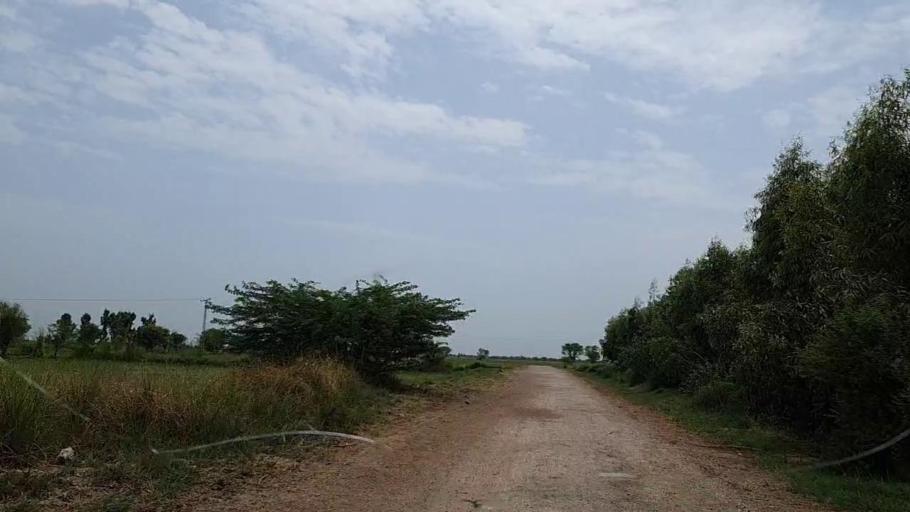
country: PK
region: Sindh
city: Tharu Shah
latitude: 26.9190
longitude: 68.0813
